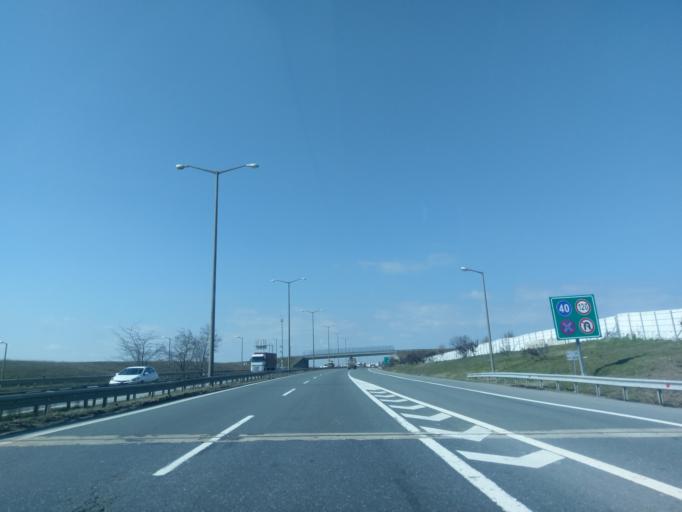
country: TR
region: Istanbul
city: Selimpasa
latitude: 41.0702
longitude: 28.3840
